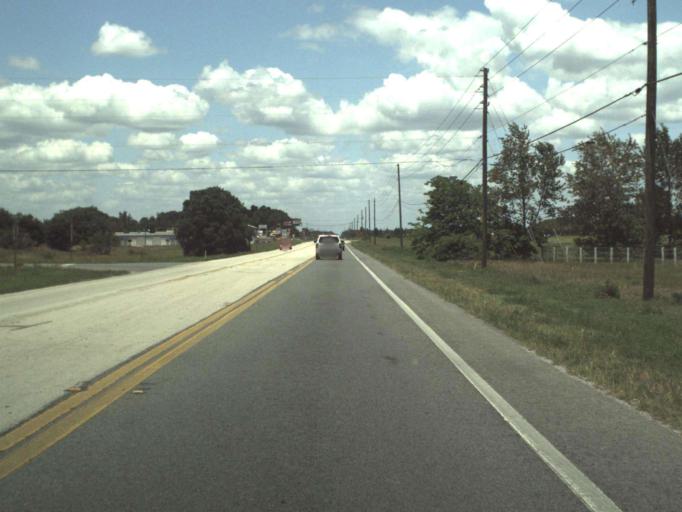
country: US
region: Florida
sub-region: Marion County
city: Silver Springs Shores
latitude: 29.0981
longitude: -82.0535
